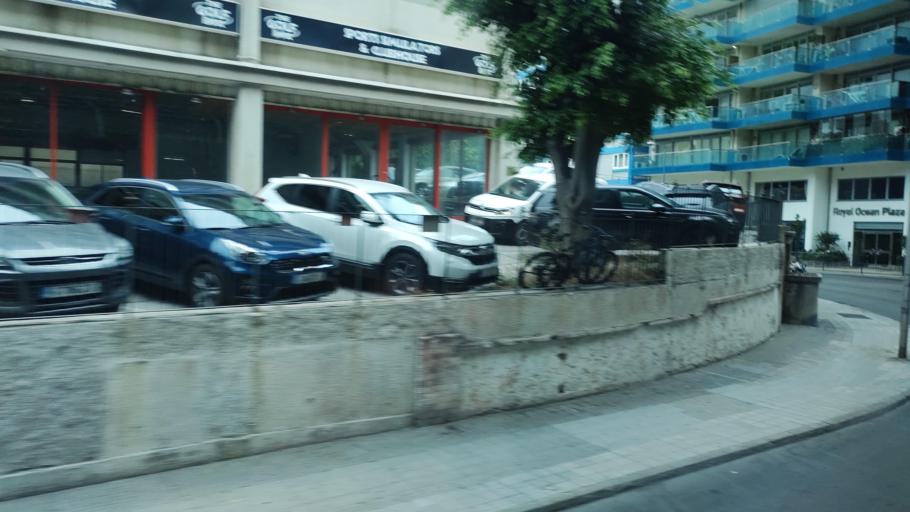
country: GI
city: Gibraltar
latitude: 36.1470
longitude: -5.3522
